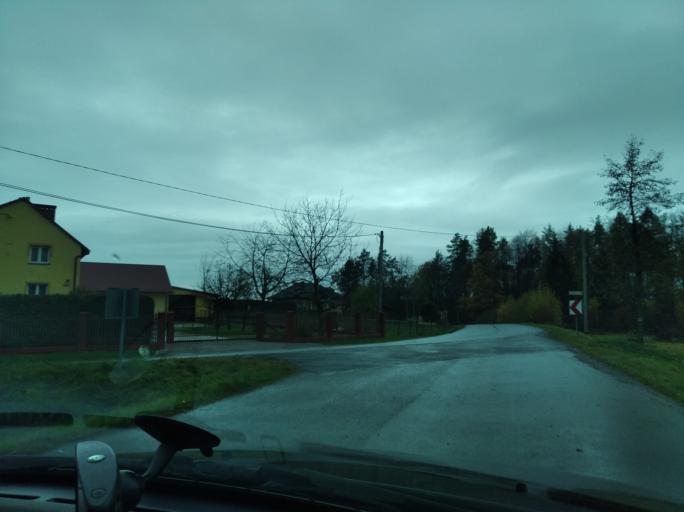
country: PL
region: Subcarpathian Voivodeship
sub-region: Powiat rzeszowski
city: Lecka
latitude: 49.9188
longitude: 22.0334
